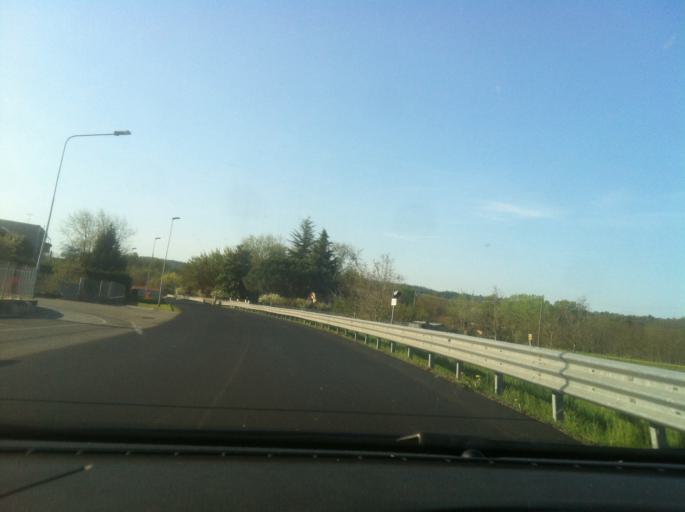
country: IT
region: Piedmont
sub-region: Provincia di Torino
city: Mercenasco
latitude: 45.3666
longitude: 7.8764
